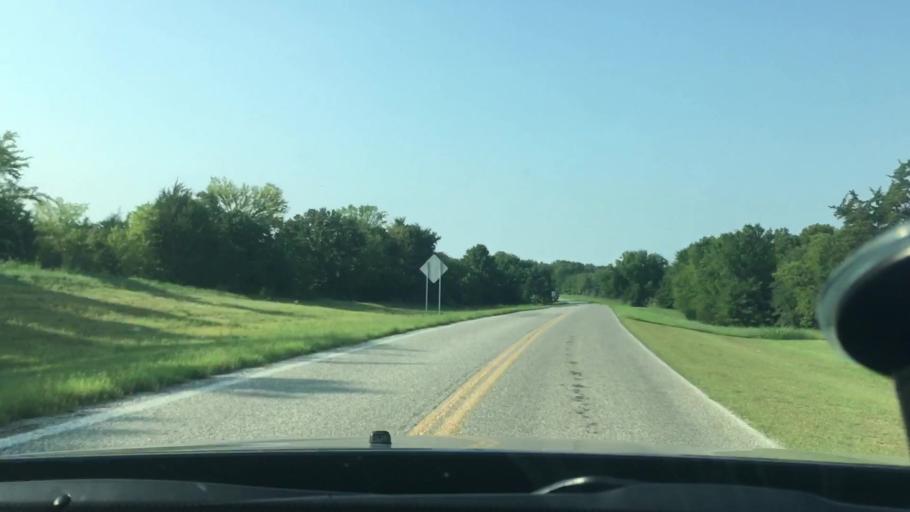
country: US
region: Oklahoma
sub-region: Johnston County
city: Tishomingo
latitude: 34.2280
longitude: -96.6351
